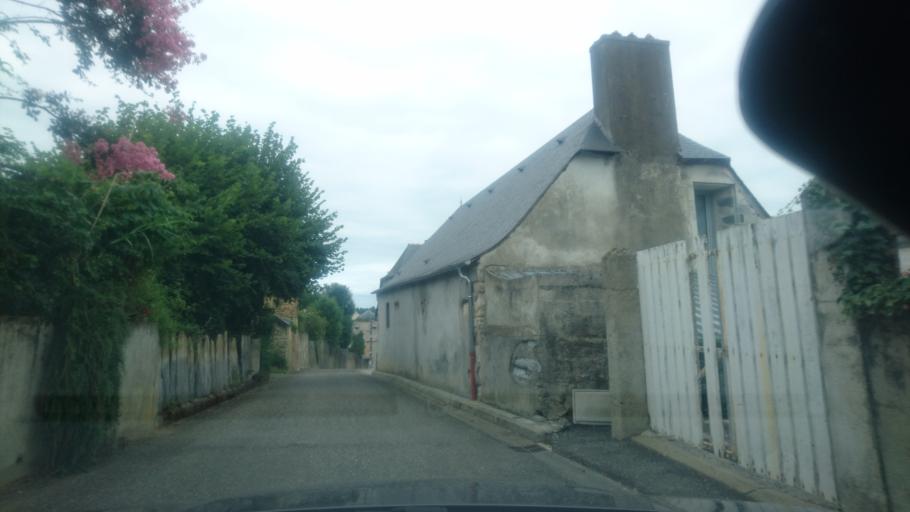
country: FR
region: Midi-Pyrenees
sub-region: Departement des Hautes-Pyrenees
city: Odos
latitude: 43.1393
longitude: 0.0385
